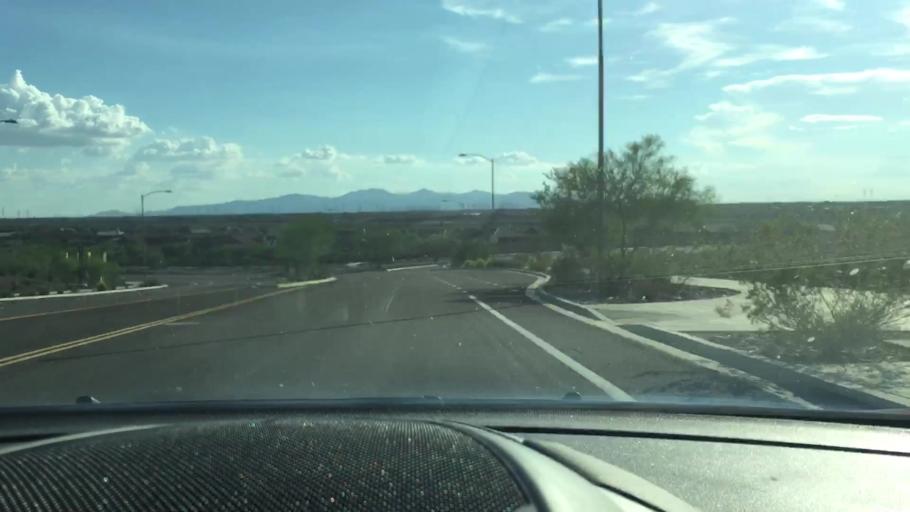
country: US
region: Arizona
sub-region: Maricopa County
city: Sun City West
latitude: 33.7237
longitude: -112.2836
